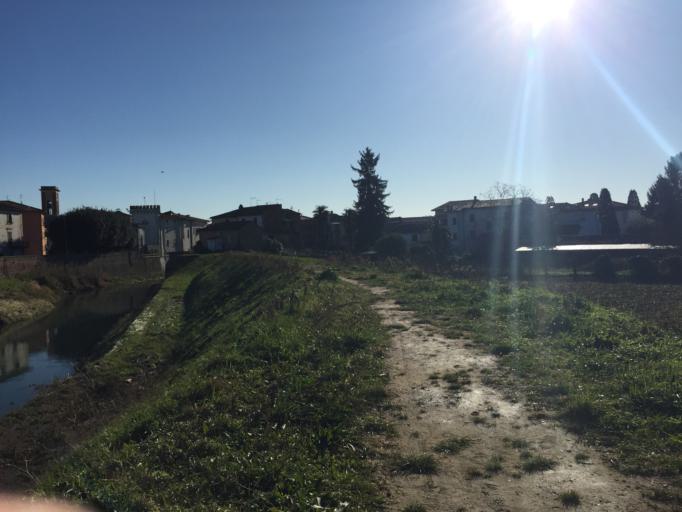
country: IT
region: Tuscany
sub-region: Provincia di Pistoia
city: Ponte Buggianese
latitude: 43.8412
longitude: 10.7456
